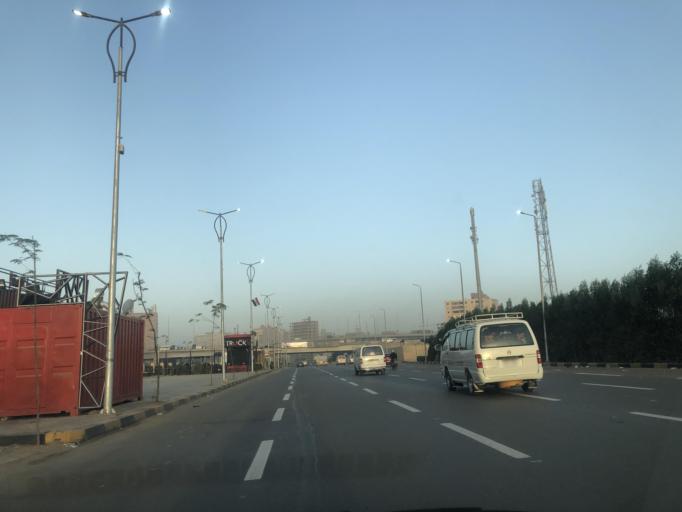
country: EG
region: Al Jizah
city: Al Jizah
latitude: 29.9736
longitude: 31.1751
